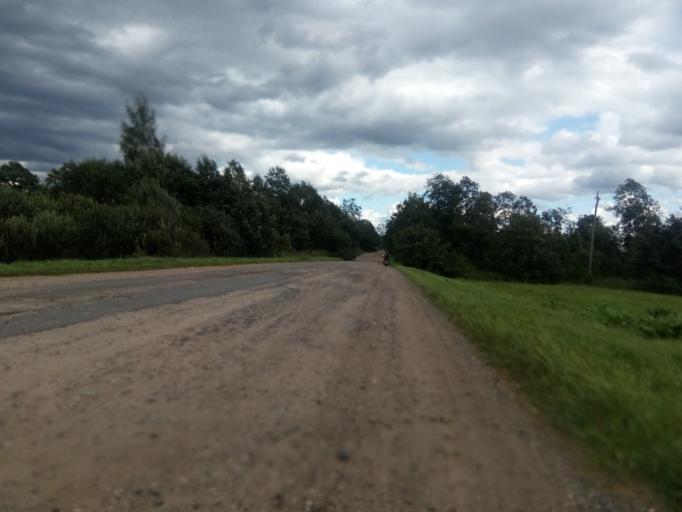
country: BY
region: Vitebsk
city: Dzisna
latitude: 55.7080
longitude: 28.3137
